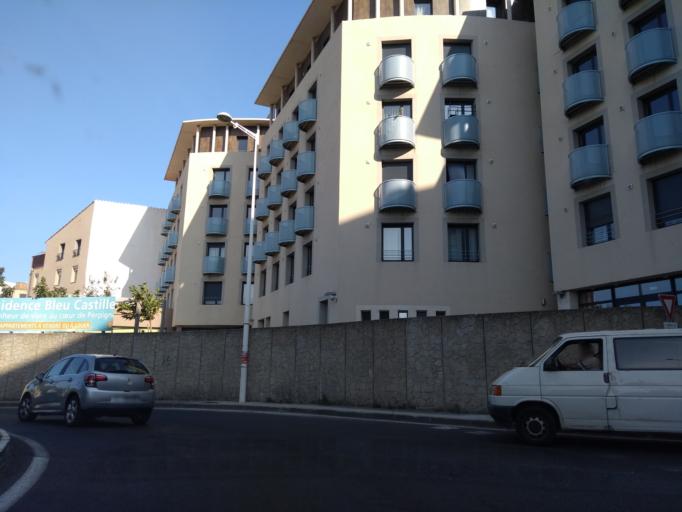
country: FR
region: Languedoc-Roussillon
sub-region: Departement des Pyrenees-Orientales
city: Perpignan
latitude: 42.7026
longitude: 2.8919
